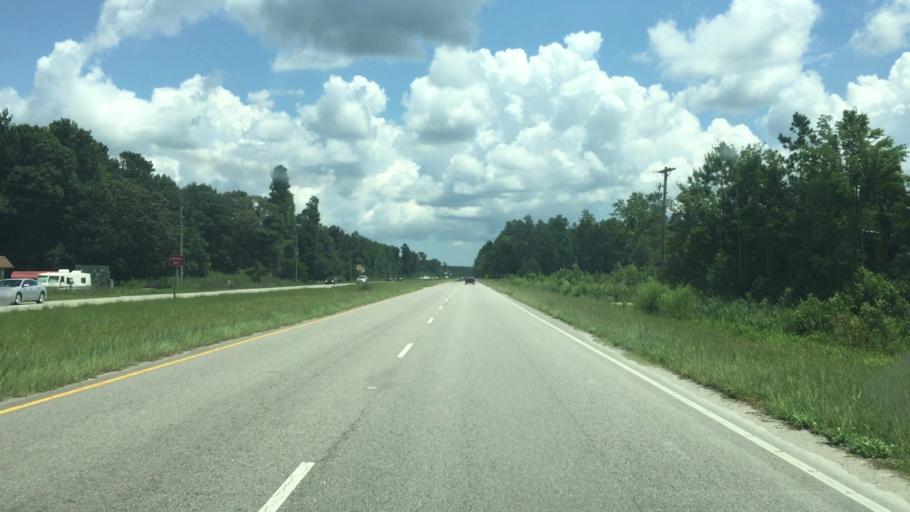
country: US
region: South Carolina
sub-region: Horry County
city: Loris
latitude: 34.0142
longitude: -78.7839
